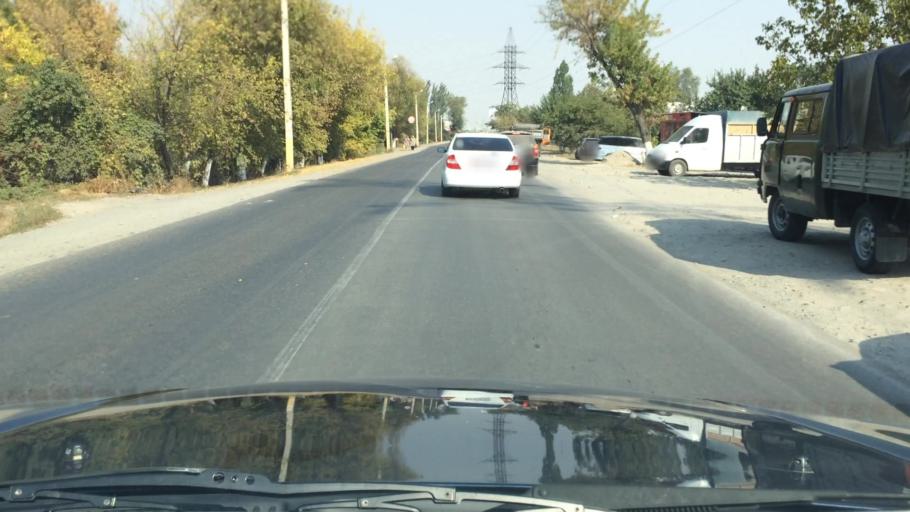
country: KG
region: Chuy
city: Lebedinovka
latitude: 42.8865
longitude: 74.6787
